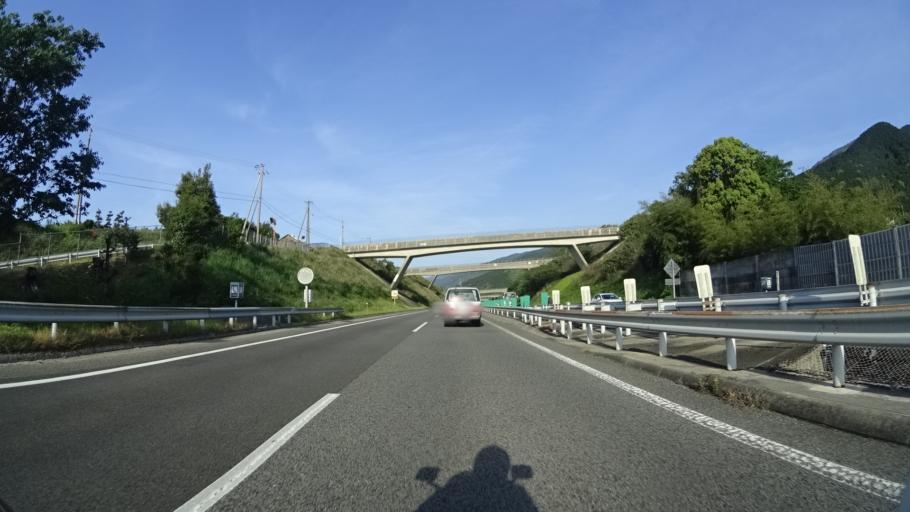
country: JP
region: Ehime
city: Kawanoecho
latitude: 33.9597
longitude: 133.4855
